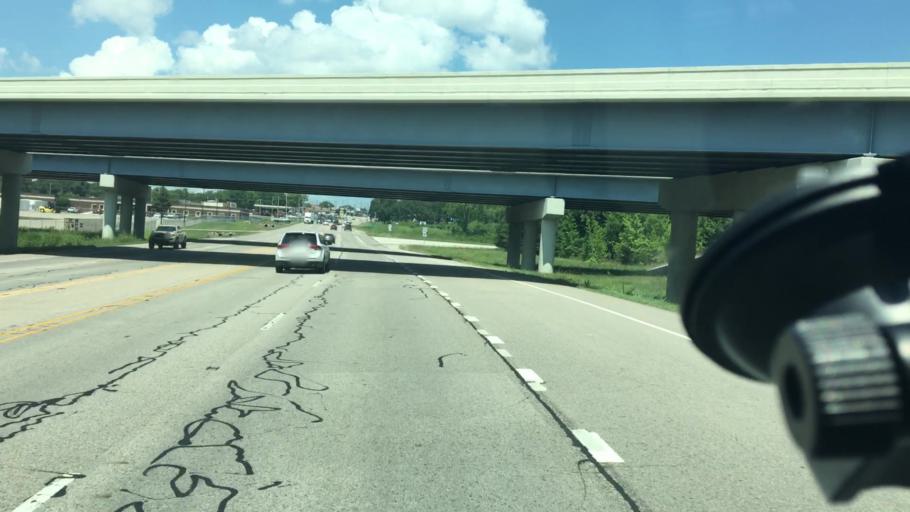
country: US
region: Arkansas
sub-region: Sebastian County
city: Barling
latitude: 35.3216
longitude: -94.2923
